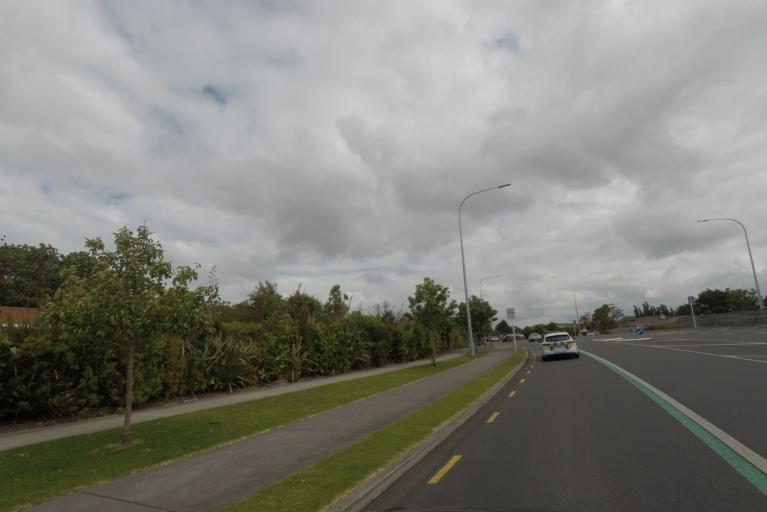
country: NZ
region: Auckland
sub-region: Auckland
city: Rothesay Bay
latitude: -36.7350
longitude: 174.6915
